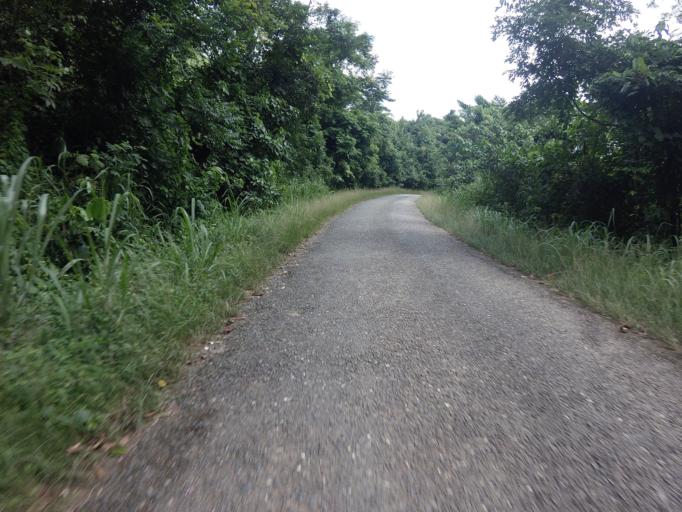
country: GH
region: Volta
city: Kpandu
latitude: 6.8366
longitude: 0.4271
